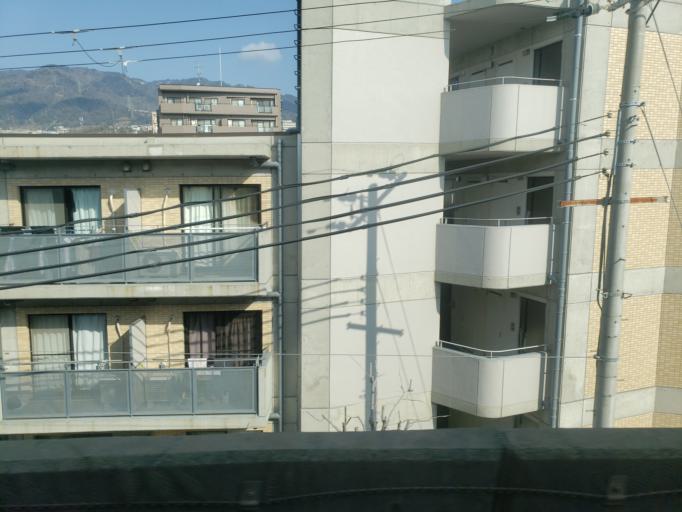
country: JP
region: Hyogo
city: Ashiya
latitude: 34.7195
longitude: 135.2524
